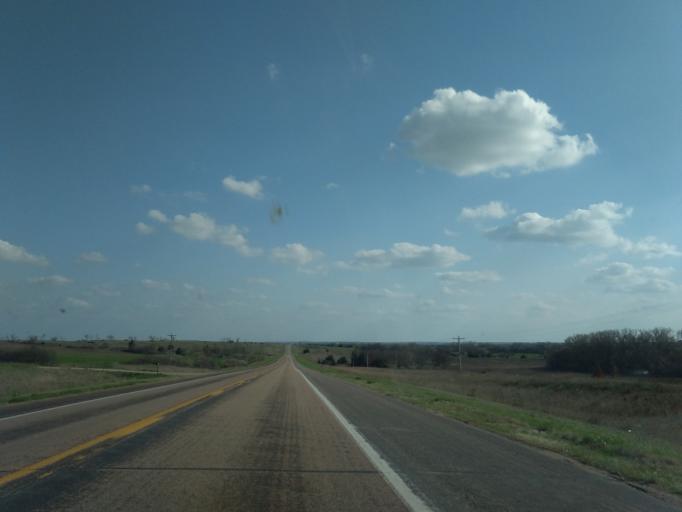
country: US
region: Nebraska
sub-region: Webster County
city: Red Cloud
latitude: 40.1393
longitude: -98.5191
